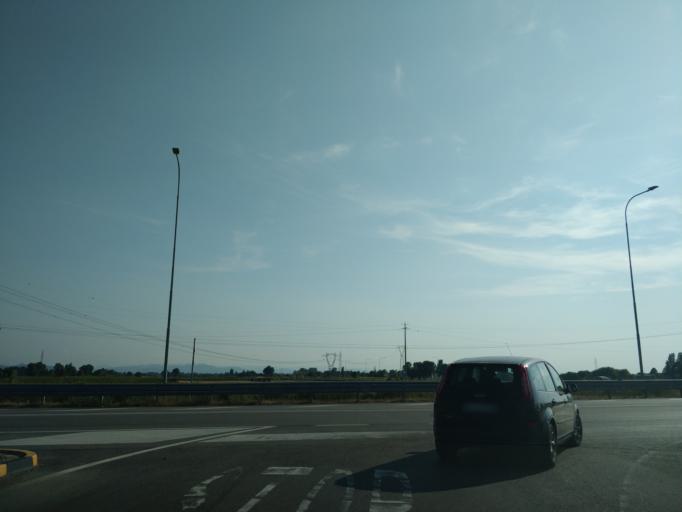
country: IT
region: Emilia-Romagna
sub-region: Provincia di Bologna
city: Castel Maggiore
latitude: 44.5998
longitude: 11.3476
